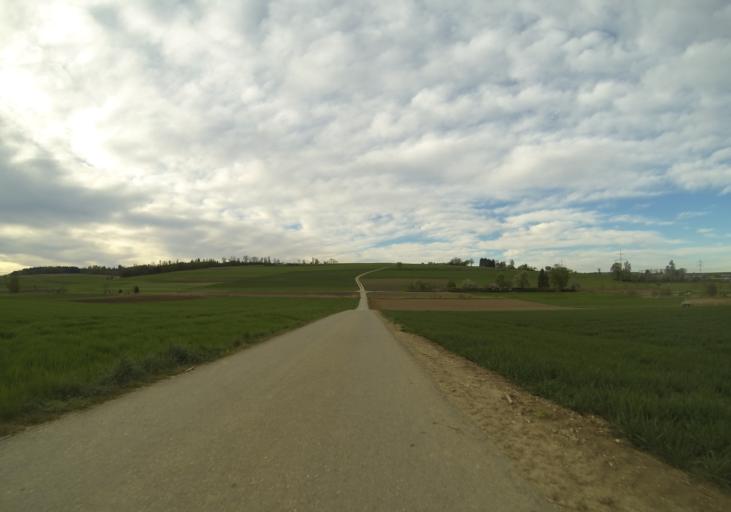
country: DE
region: Baden-Wuerttemberg
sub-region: Tuebingen Region
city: Erbach
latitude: 48.3284
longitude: 9.8703
